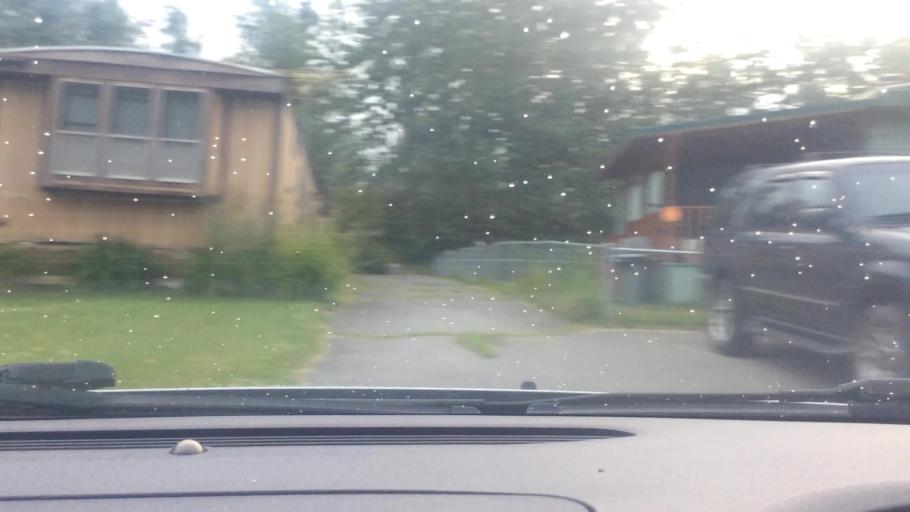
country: US
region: Alaska
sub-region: Anchorage Municipality
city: Elmendorf Air Force Base
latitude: 61.1992
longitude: -149.7254
